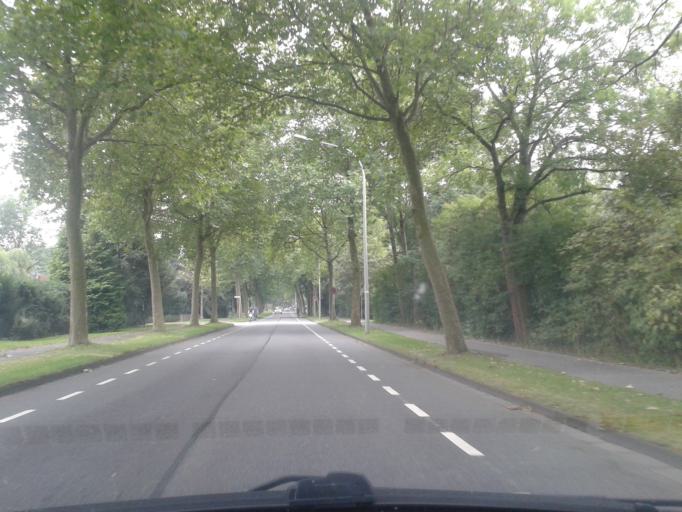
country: DE
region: North Rhine-Westphalia
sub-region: Regierungsbezirk Detmold
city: Paderborn
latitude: 51.7454
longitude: 8.7468
